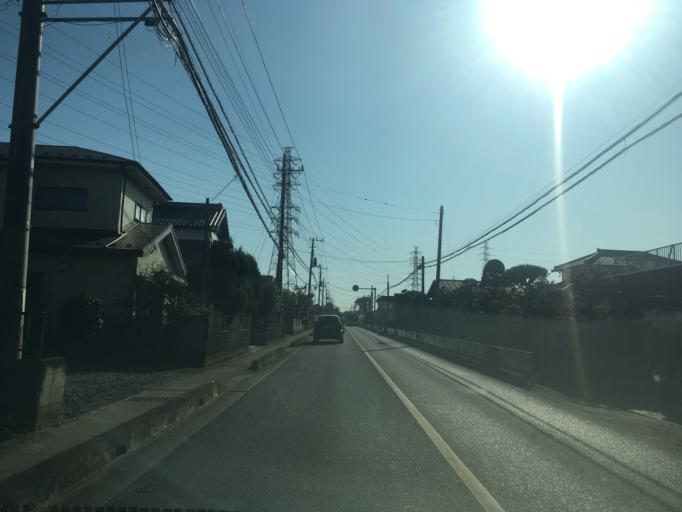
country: JP
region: Saitama
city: Kawagoe
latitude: 35.8693
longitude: 139.4726
